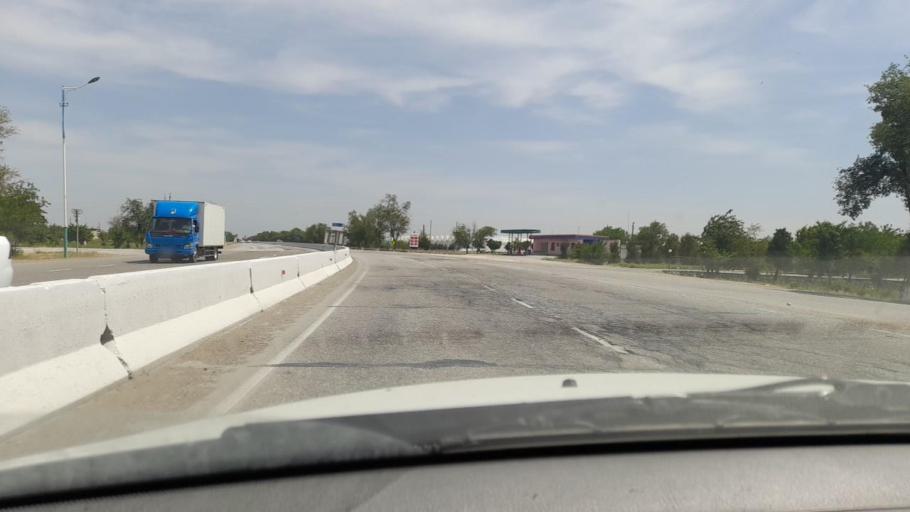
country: UZ
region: Navoiy
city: Qiziltepa
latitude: 40.0538
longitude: 64.8721
